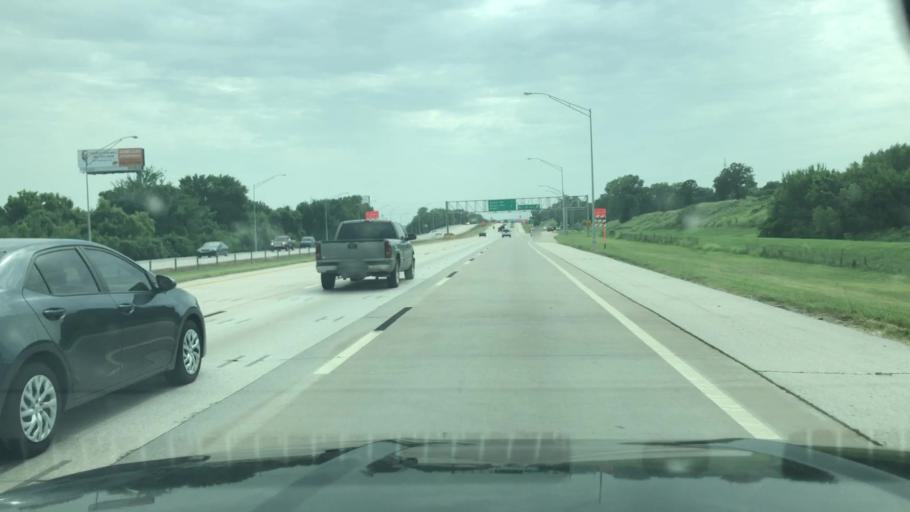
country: US
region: Oklahoma
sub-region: Tulsa County
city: Sand Springs
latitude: 36.1450
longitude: -96.0774
